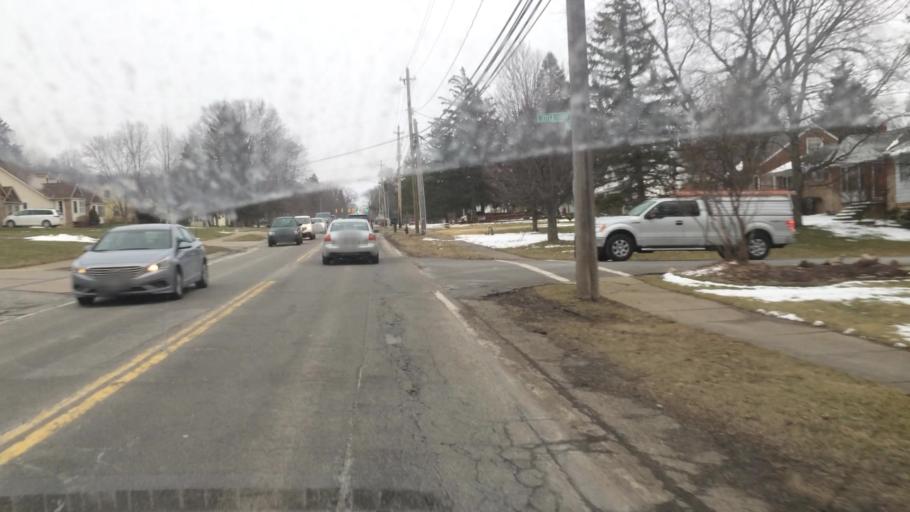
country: US
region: Ohio
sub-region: Cuyahoga County
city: Independence
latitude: 41.3447
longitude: -81.6620
